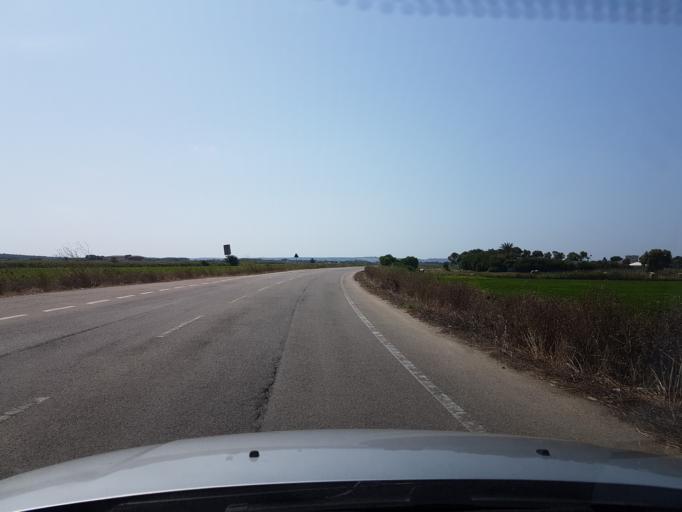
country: IT
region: Sardinia
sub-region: Provincia di Oristano
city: Cabras
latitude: 39.9179
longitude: 8.5289
